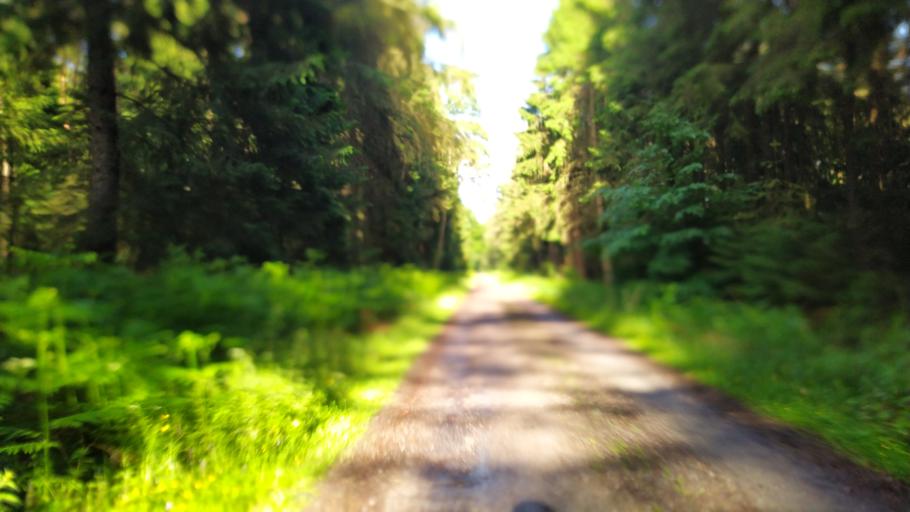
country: DE
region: Lower Saxony
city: Deinstedt
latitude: 53.4390
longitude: 9.2269
